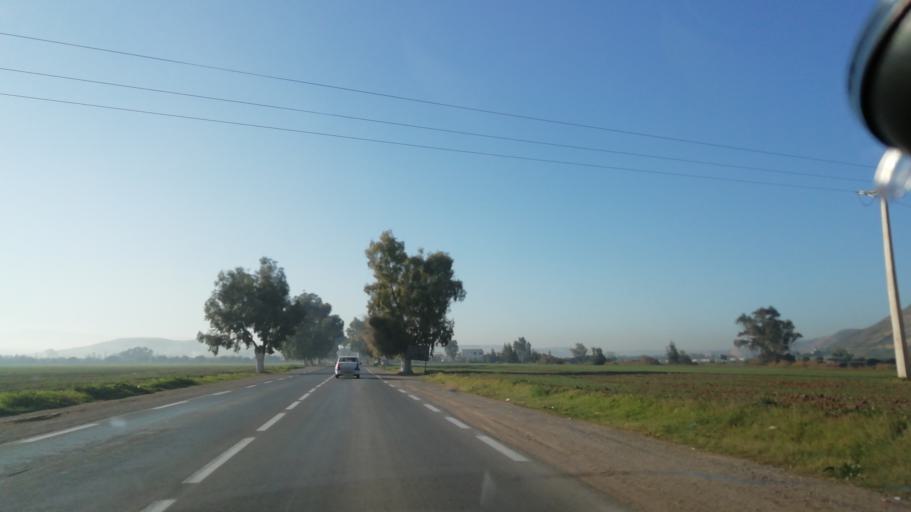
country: DZ
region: Tlemcen
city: Remchi
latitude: 35.0519
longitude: -1.5022
